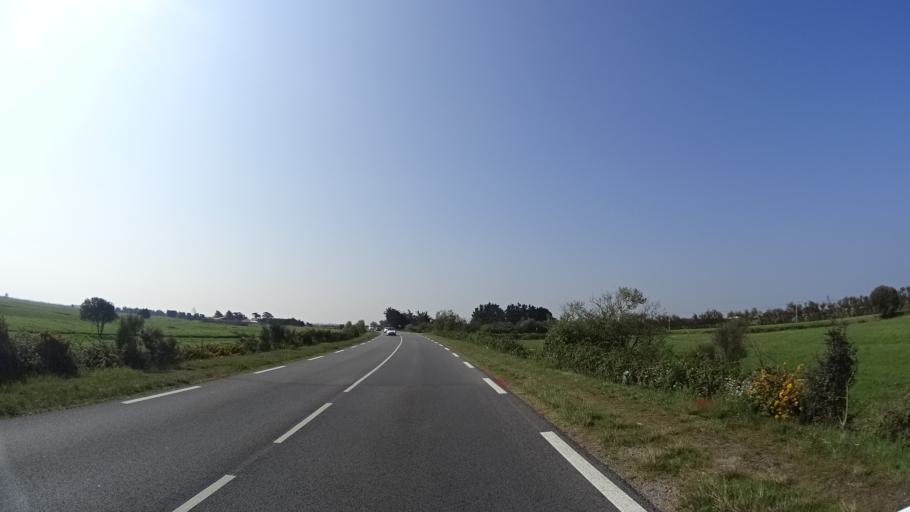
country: FR
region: Pays de la Loire
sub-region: Departement de la Loire-Atlantique
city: Bourgneuf-en-Retz
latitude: 47.0331
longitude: -1.9633
